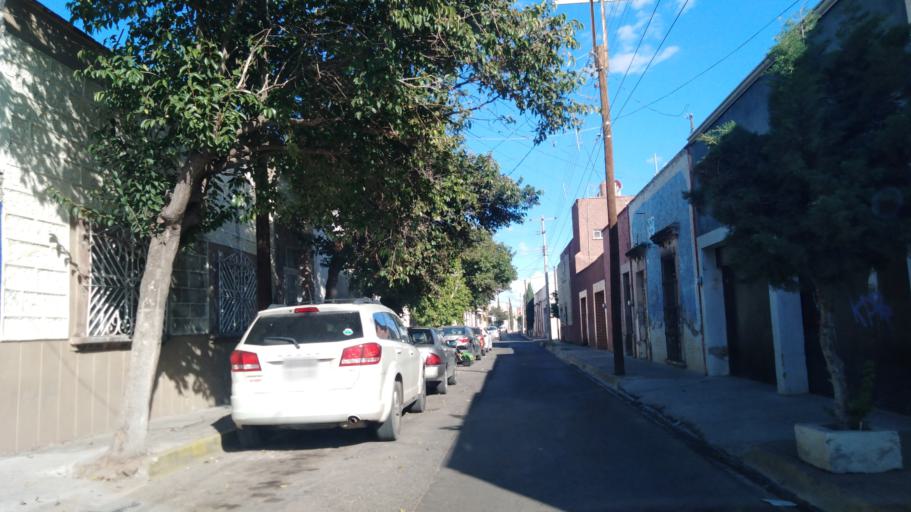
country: MX
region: Durango
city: Victoria de Durango
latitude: 24.0334
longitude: -104.6738
